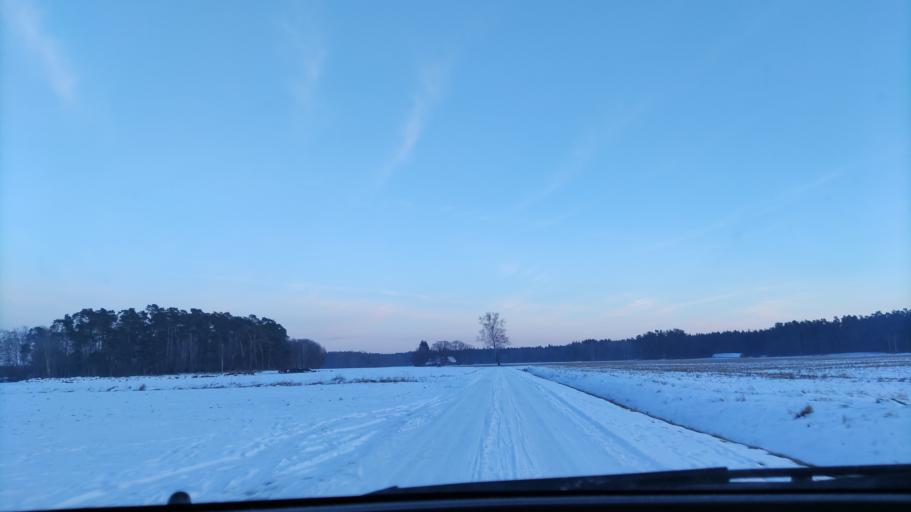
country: DE
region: Lower Saxony
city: Neetze
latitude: 53.2933
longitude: 10.6741
